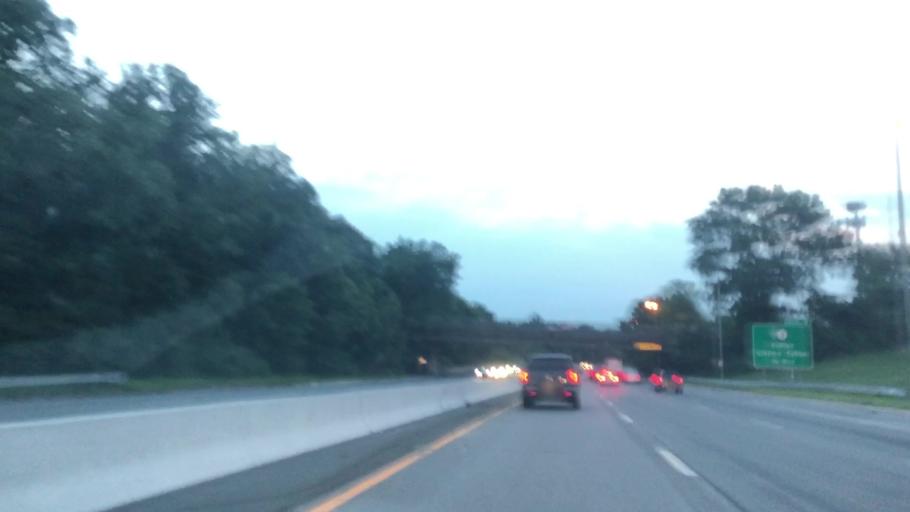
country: US
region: New Jersey
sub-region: Bergen County
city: Rutherford
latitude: 40.8333
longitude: -74.1231
